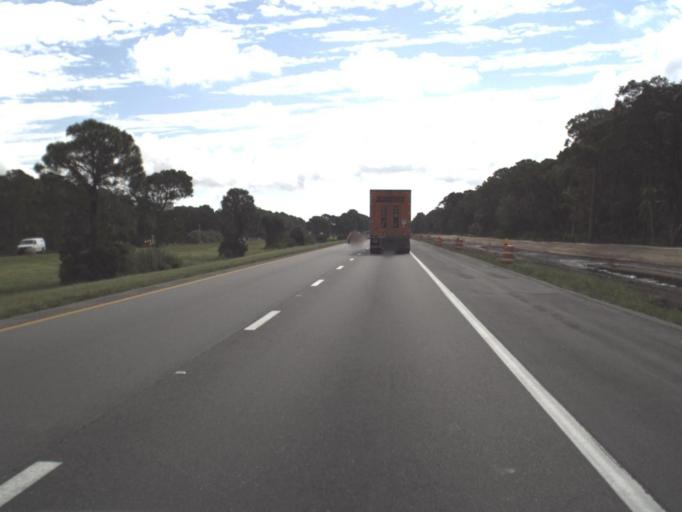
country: US
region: Florida
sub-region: Sarasota County
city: Warm Mineral Springs
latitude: 27.0997
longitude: -82.2532
